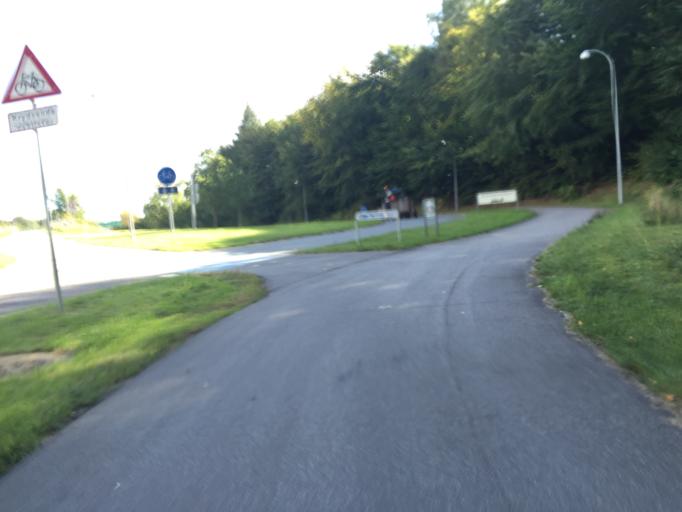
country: DK
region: Capital Region
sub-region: Herlev Kommune
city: Herlev
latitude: 55.7665
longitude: 12.4297
